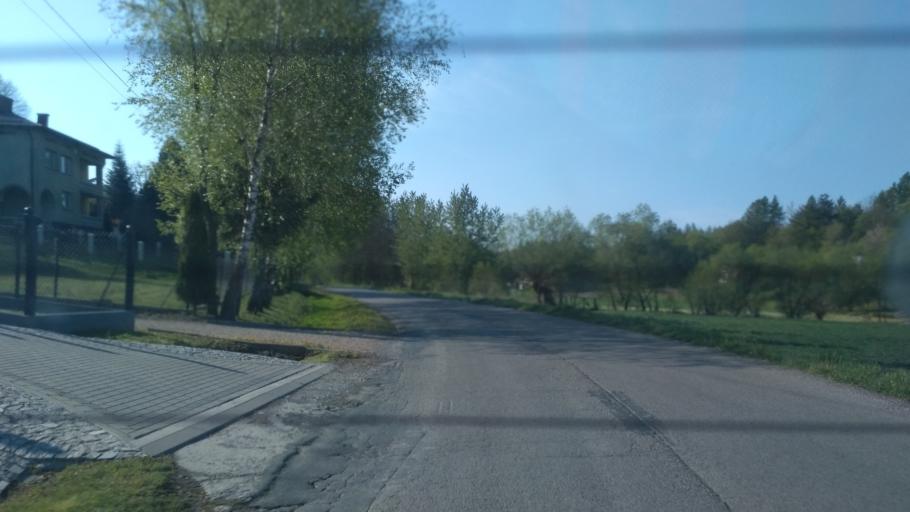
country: PL
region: Subcarpathian Voivodeship
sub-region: Powiat jaroslawski
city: Pruchnik
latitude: 49.8738
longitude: 22.5651
